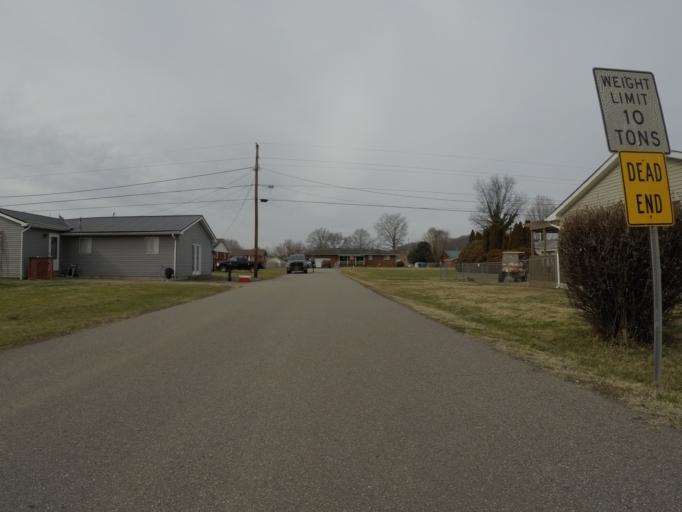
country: US
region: West Virginia
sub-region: Cabell County
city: Pea Ridge
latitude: 38.4475
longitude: -82.3534
